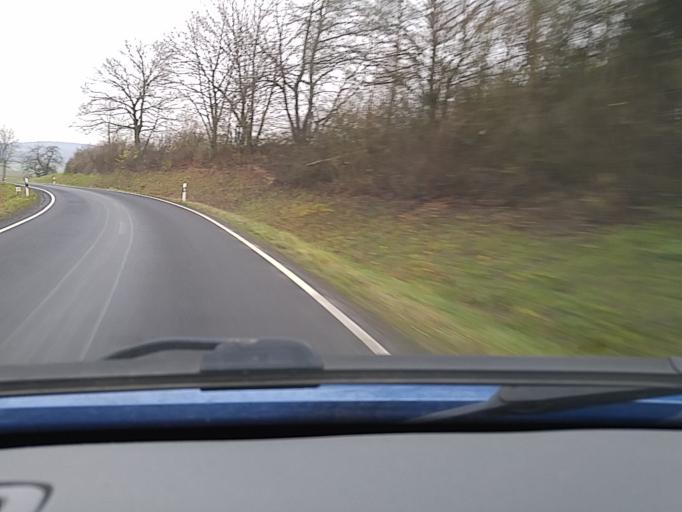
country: DE
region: Hesse
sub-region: Regierungsbezirk Darmstadt
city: Altenstadt
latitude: 50.3058
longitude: 8.9328
